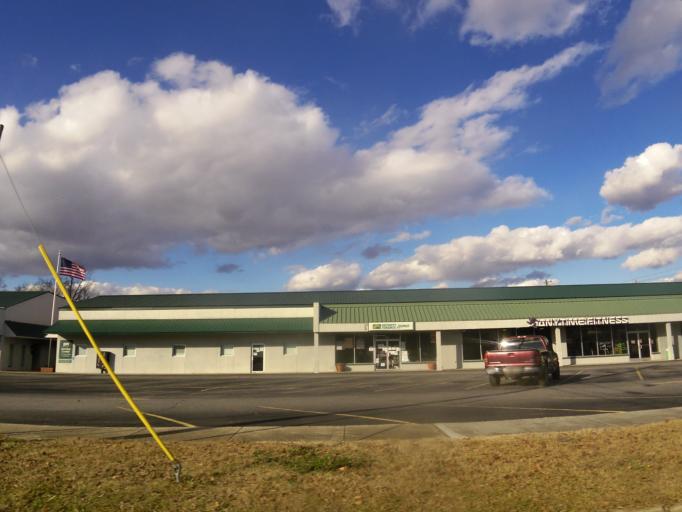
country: US
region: South Carolina
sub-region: Clarendon County
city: Manning
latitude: 33.6967
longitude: -80.2113
